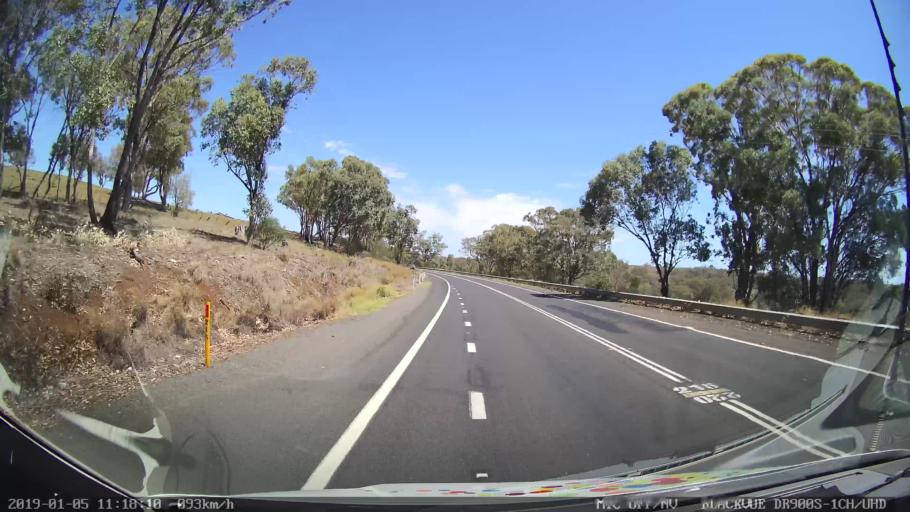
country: AU
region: New South Wales
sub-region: Warrumbungle Shire
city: Coonabarabran
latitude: -31.3171
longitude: 149.3070
